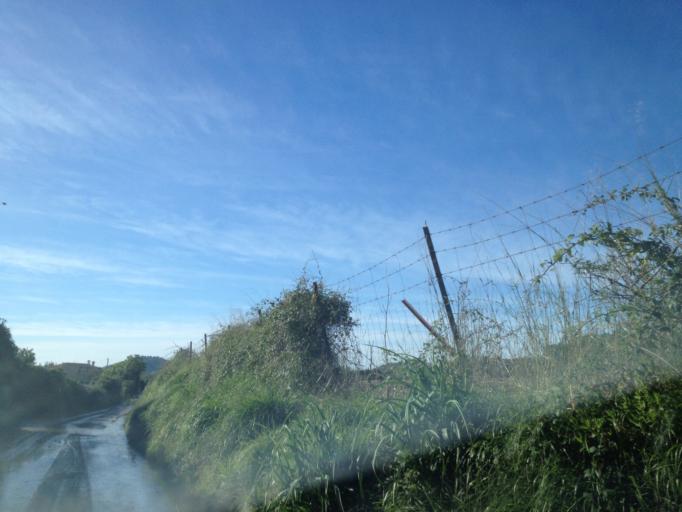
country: ES
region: Balearic Islands
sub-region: Illes Balears
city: Sineu
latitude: 39.6452
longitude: 3.0334
